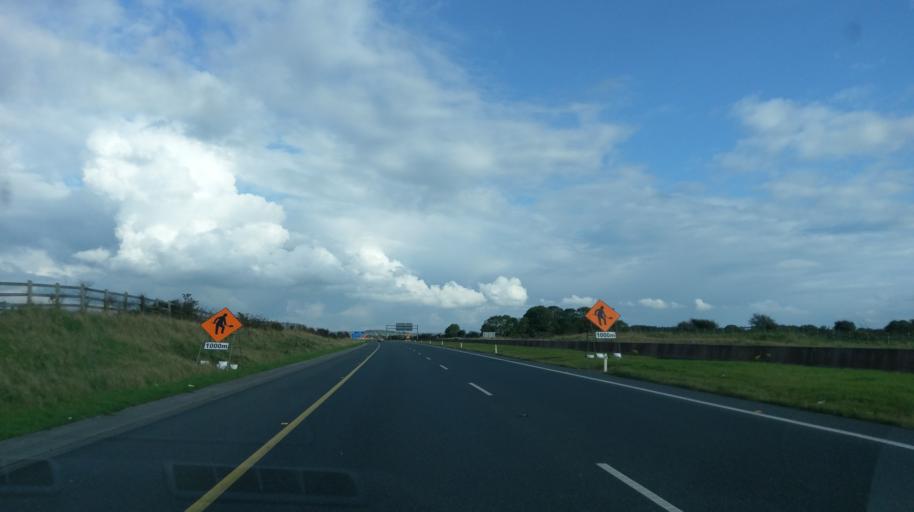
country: IE
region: Connaught
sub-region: County Galway
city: Oranmore
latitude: 53.2963
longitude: -8.9067
